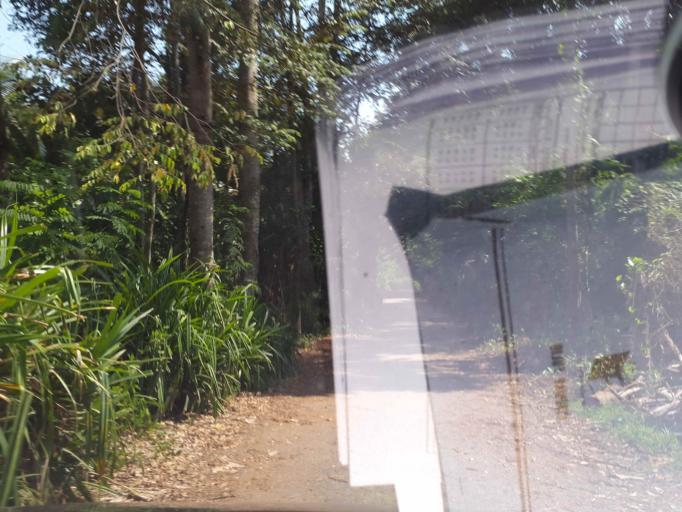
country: ID
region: West Nusa Tenggara
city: Karangkebon Timur
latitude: -8.6797
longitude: 116.0905
